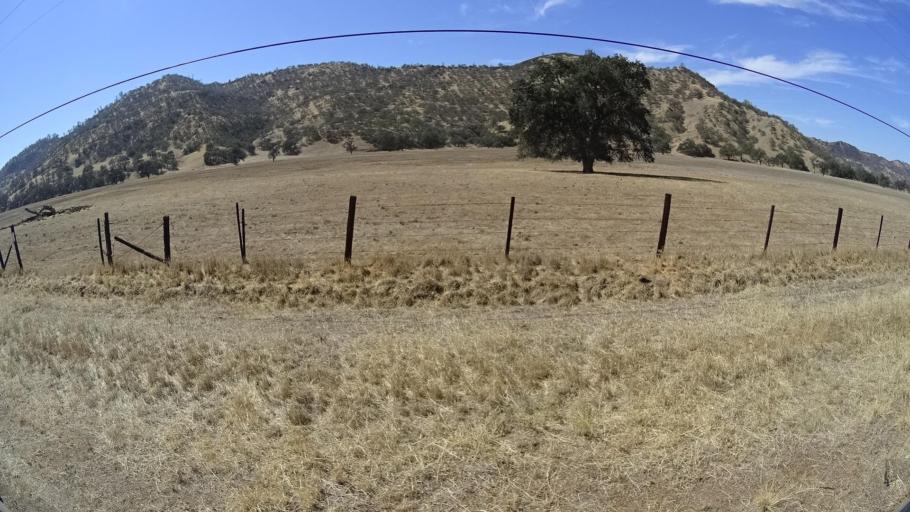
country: US
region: California
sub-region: Monterey County
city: King City
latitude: 36.1488
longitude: -120.7584
